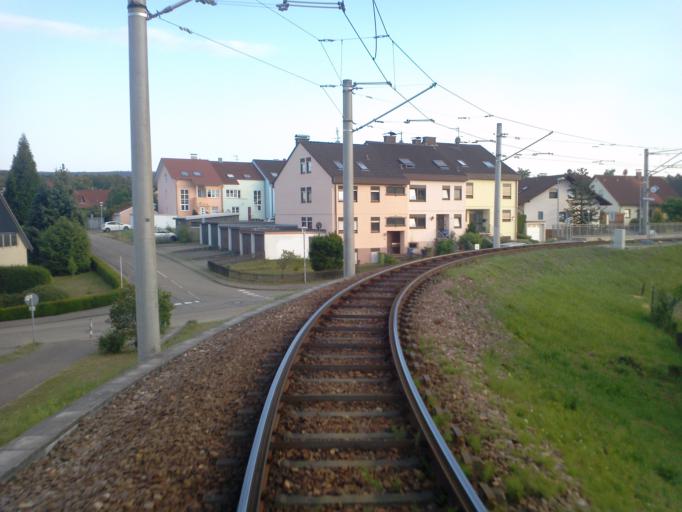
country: DE
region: Baden-Wuerttemberg
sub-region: Karlsruhe Region
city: Dobel
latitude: 48.8665
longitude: 8.5112
